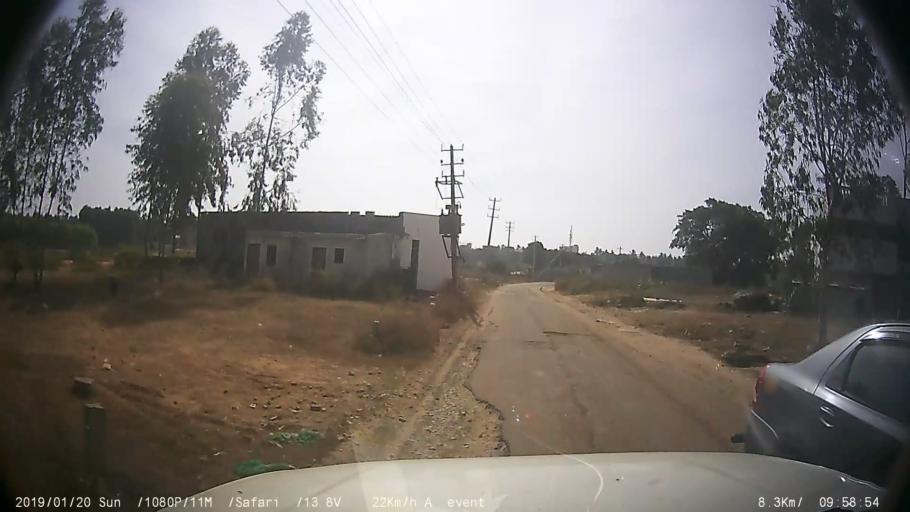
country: IN
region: Karnataka
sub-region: Bangalore Urban
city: Anekal
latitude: 12.8243
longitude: 77.6361
